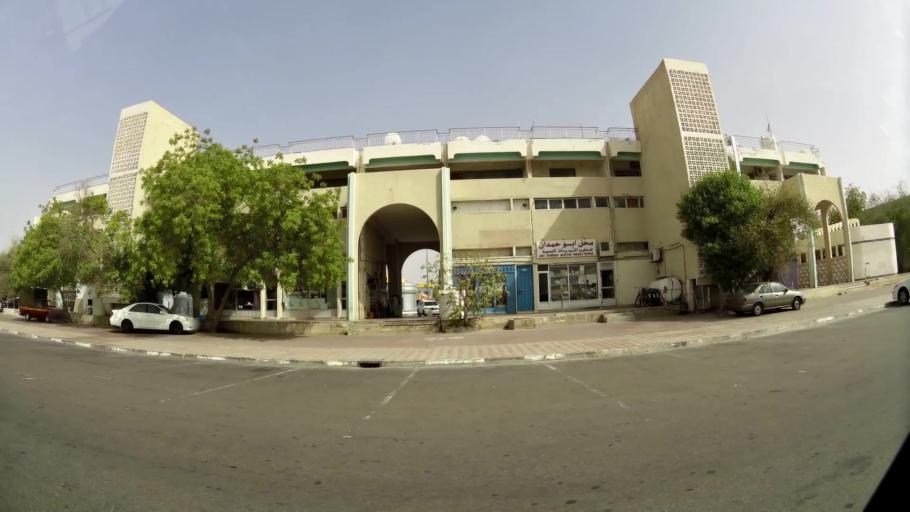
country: AE
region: Abu Dhabi
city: Al Ain
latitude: 24.1852
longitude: 55.6281
